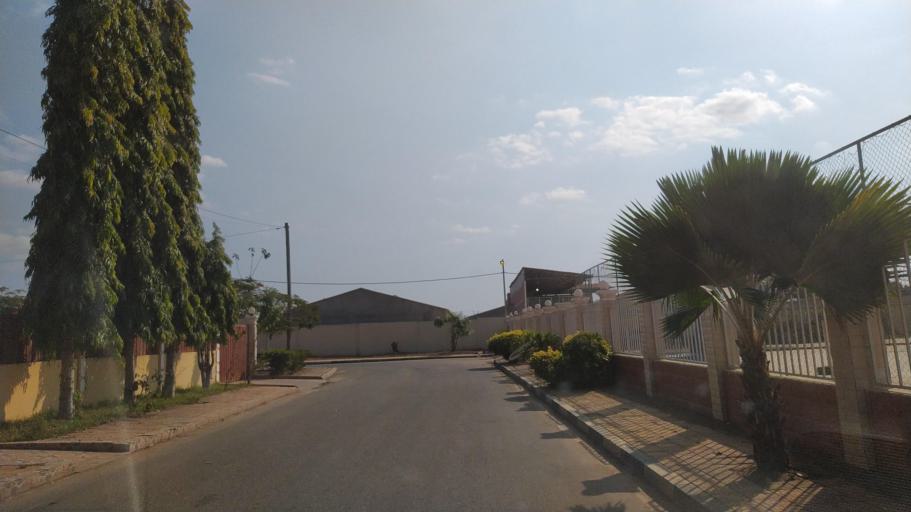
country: AO
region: Luanda
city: Luanda
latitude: -8.8914
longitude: 13.2575
